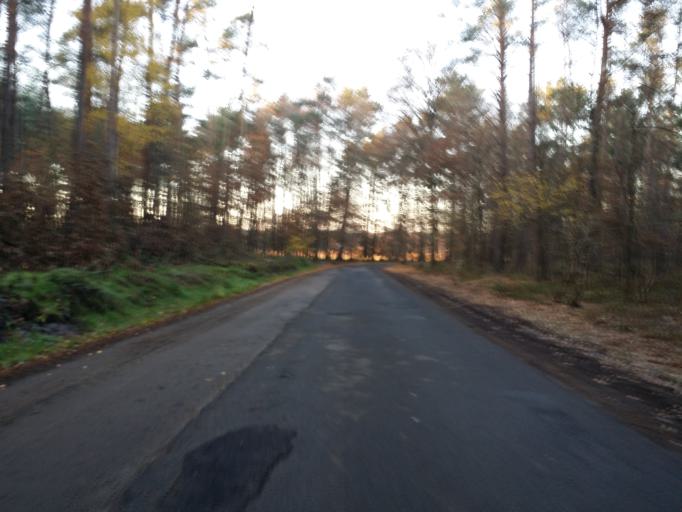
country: DE
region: Lower Saxony
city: Ahausen
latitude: 53.0828
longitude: 9.3036
